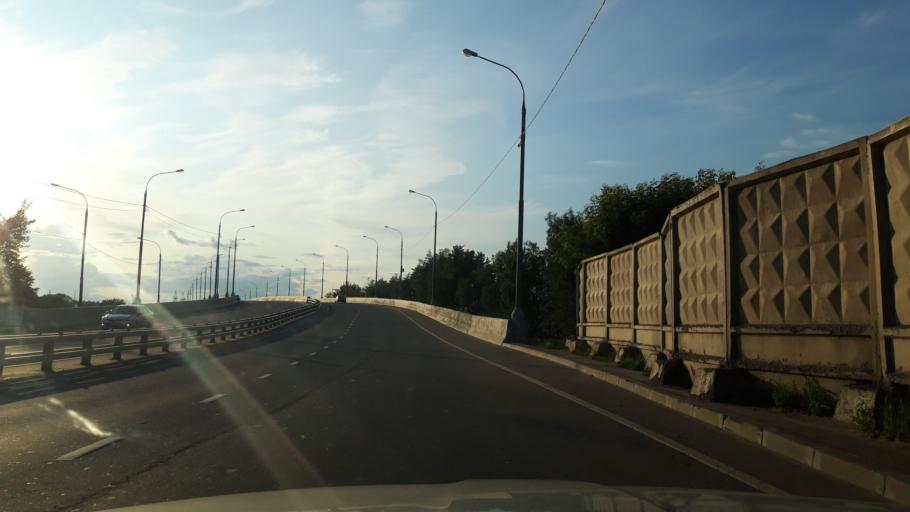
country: RU
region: Moscow
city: Zelenograd
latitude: 55.9933
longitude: 37.1649
